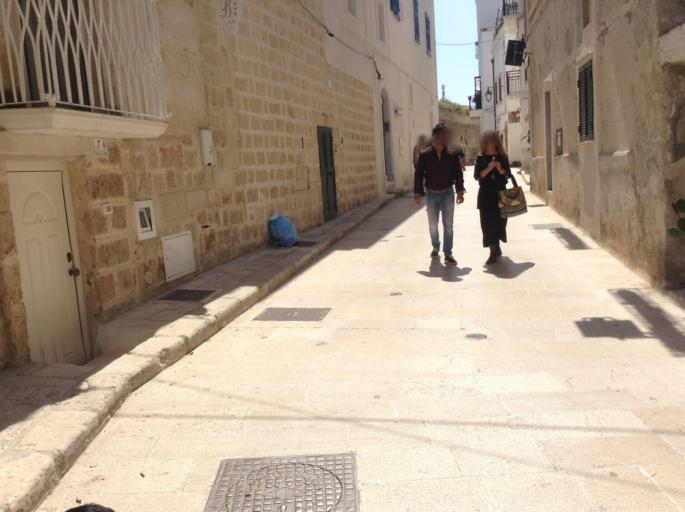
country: IT
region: Apulia
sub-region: Provincia di Bari
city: Monopoli
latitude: 40.9519
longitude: 17.3063
